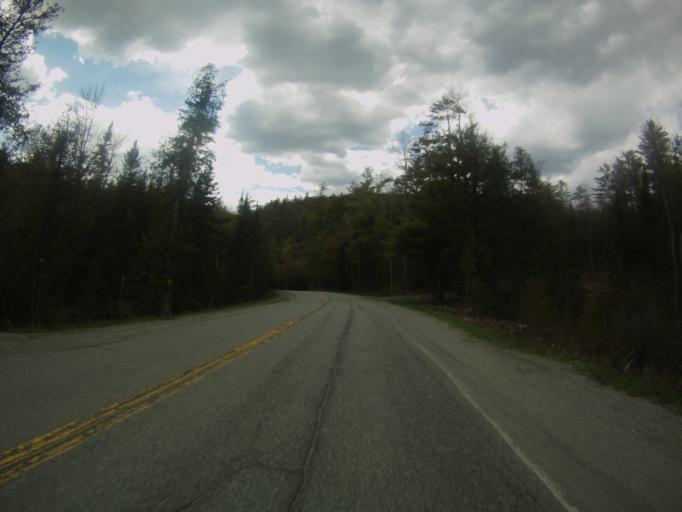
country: US
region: New York
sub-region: Essex County
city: Mineville
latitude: 44.0778
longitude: -73.6220
